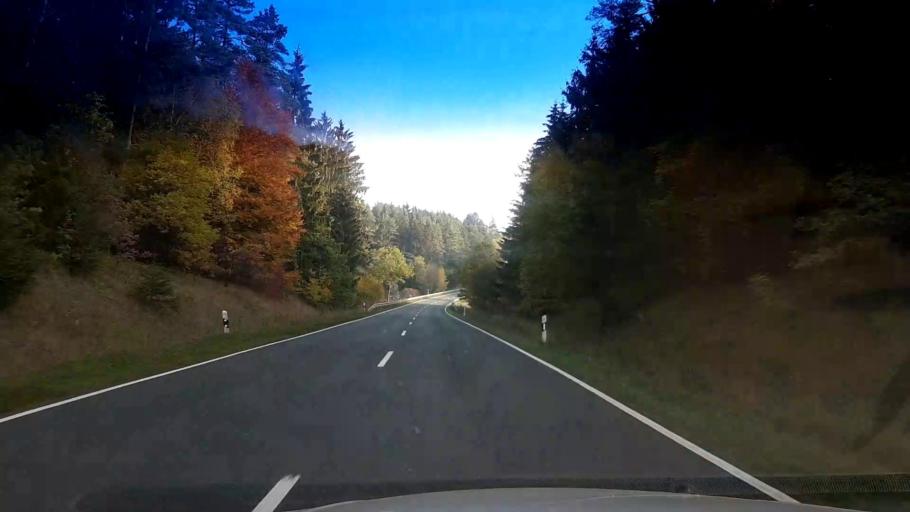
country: DE
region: Bavaria
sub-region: Upper Franconia
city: Stadelhofen
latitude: 50.0025
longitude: 11.1634
